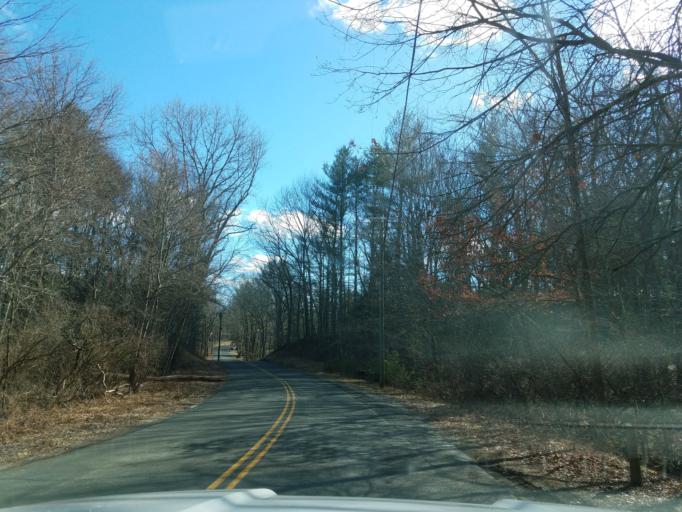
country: US
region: Connecticut
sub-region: Windham County
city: North Grosvenor Dale
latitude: 42.0121
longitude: -71.8719
